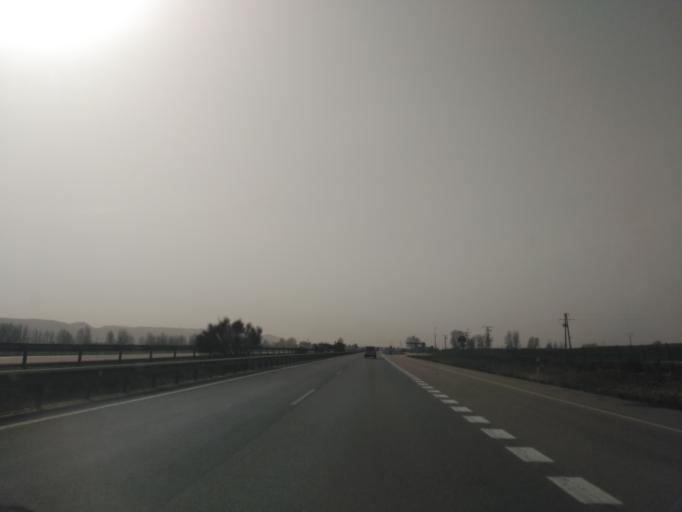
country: ES
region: Castille and Leon
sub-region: Provincia de Valladolid
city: Cabezon
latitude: 41.7777
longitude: -4.6166
